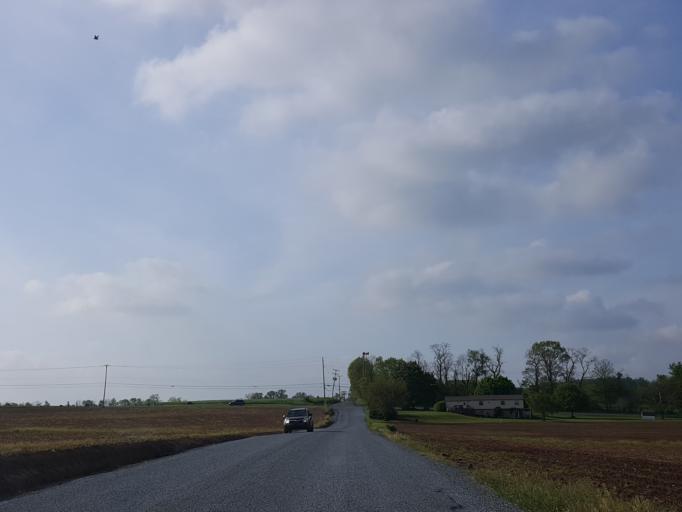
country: US
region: Pennsylvania
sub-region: Lebanon County
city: Campbelltown
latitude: 40.2258
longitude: -76.5764
